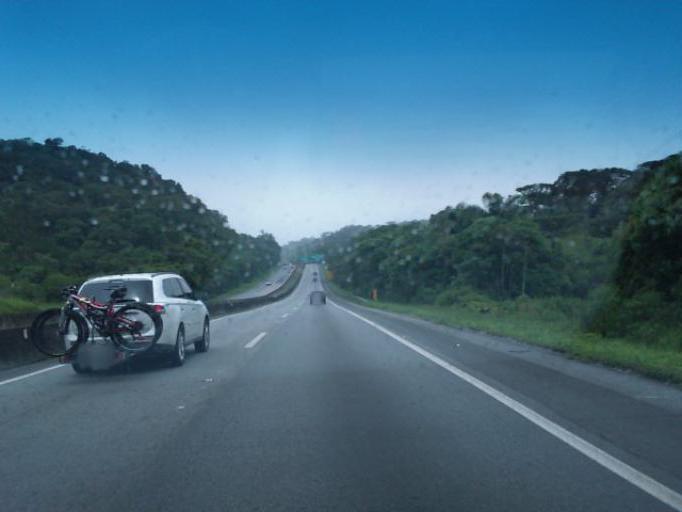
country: BR
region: Parana
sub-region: Campina Grande Do Sul
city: Campina Grande do Sul
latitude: -25.3044
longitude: -48.9541
